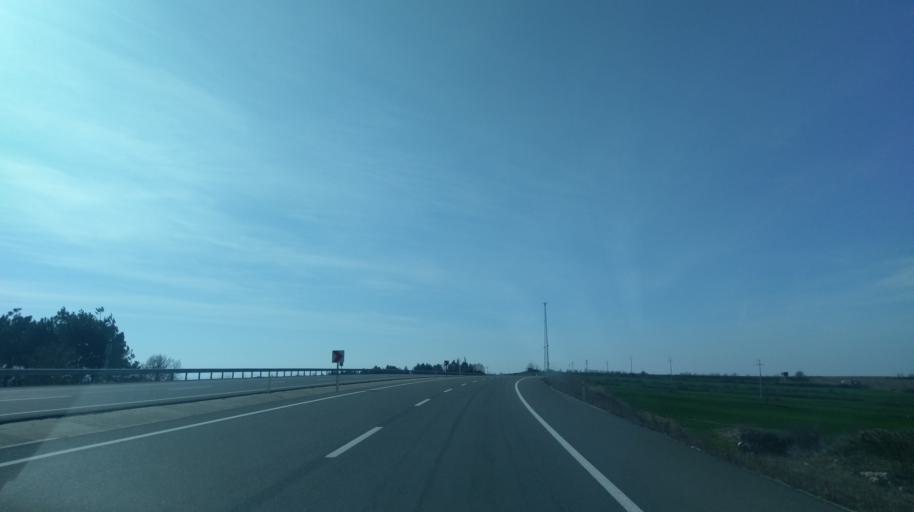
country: TR
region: Edirne
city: Hamidiye
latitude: 41.0818
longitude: 26.6395
